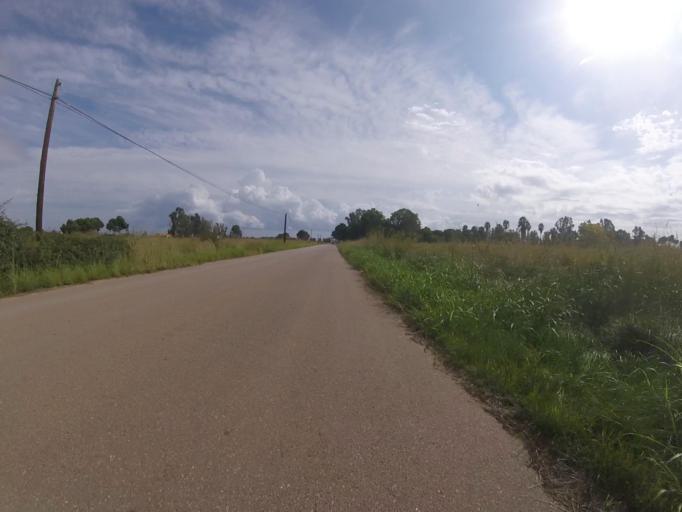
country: ES
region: Valencia
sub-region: Provincia de Castello
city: Orpesa/Oropesa del Mar
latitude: 40.1324
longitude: 0.1604
